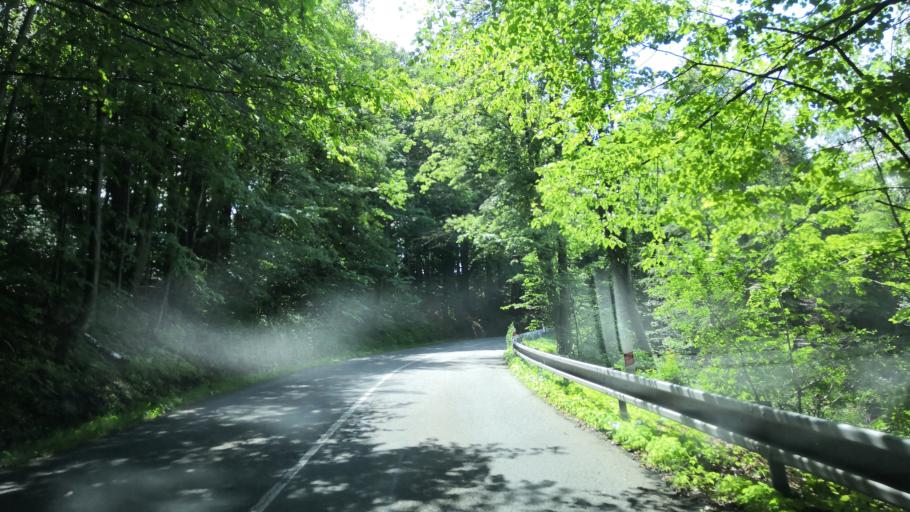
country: CZ
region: Zlin
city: Valasska Bystrice
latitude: 49.4296
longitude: 18.1285
